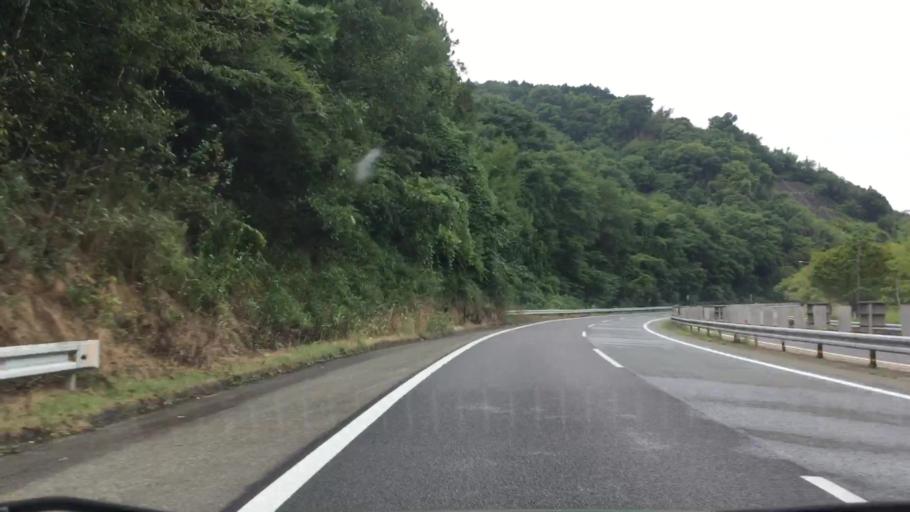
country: JP
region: Hiroshima
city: Shobara
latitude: 34.8942
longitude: 133.2449
